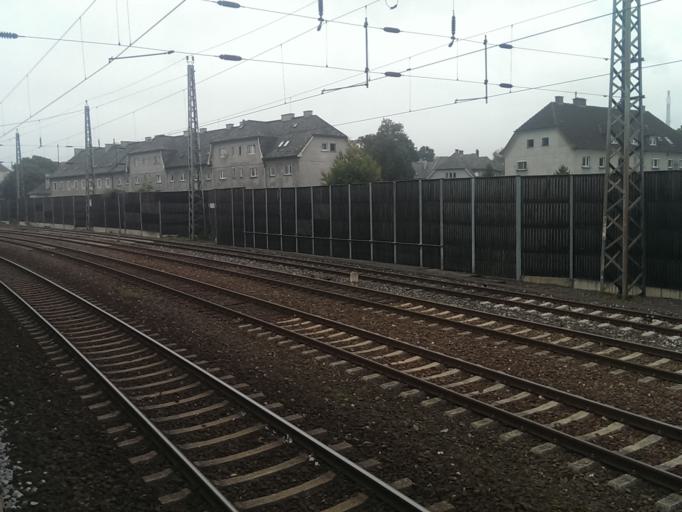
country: AT
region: Upper Austria
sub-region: Linz Stadt
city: Linz
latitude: 48.2909
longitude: 14.3127
